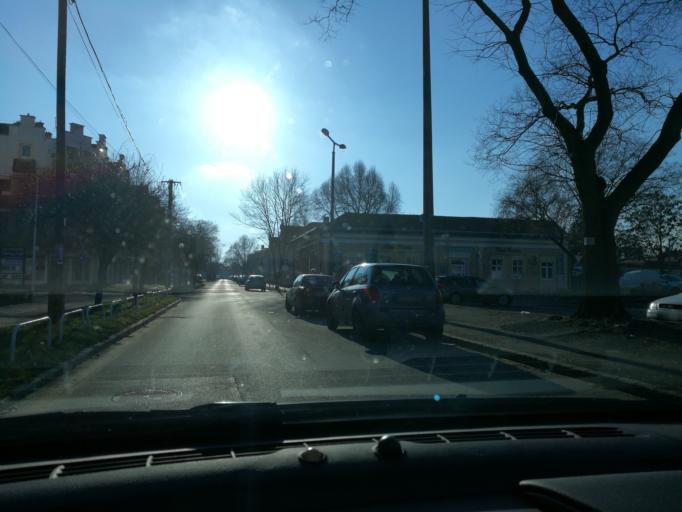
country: HU
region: Szabolcs-Szatmar-Bereg
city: Nyiregyhaza
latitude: 47.9583
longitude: 21.7105
